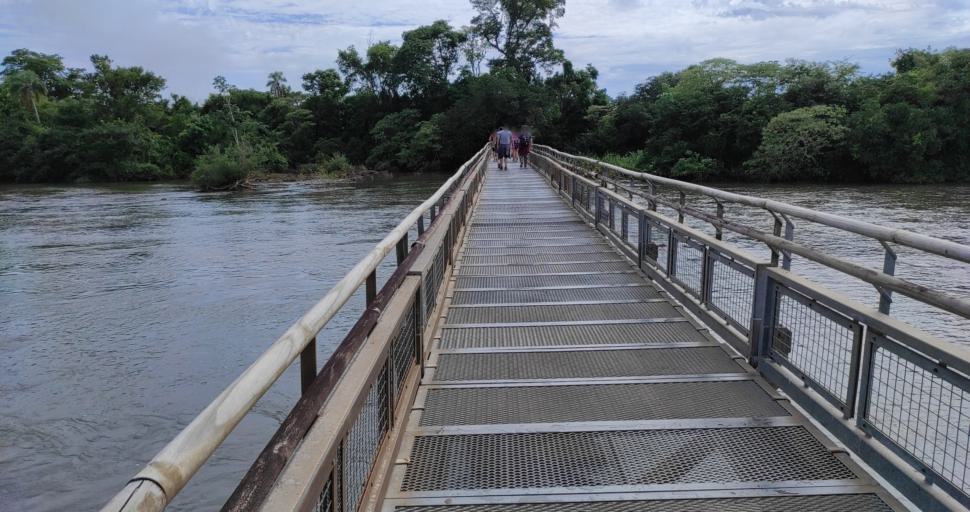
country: AR
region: Misiones
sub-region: Departamento de Iguazu
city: Puerto Iguazu
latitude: -25.6975
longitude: -54.4398
